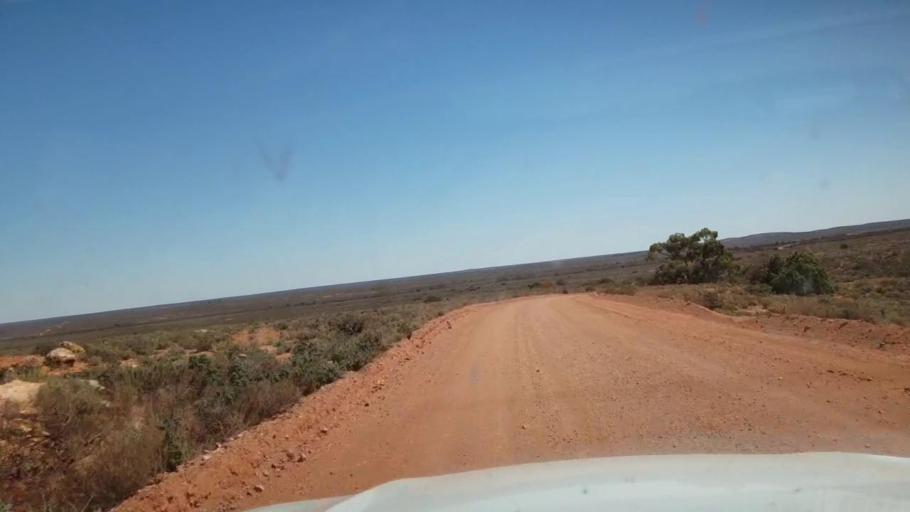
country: AU
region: South Australia
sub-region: Whyalla
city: Whyalla
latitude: -32.6854
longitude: 137.1221
